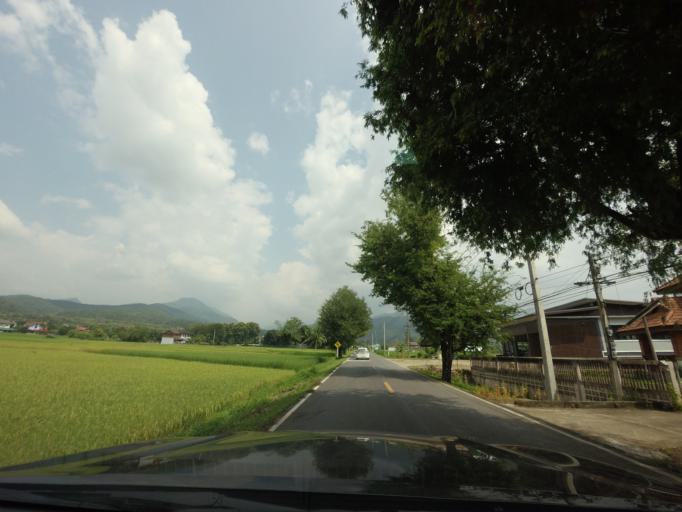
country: TH
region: Nan
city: Pua
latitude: 19.1745
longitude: 100.9400
